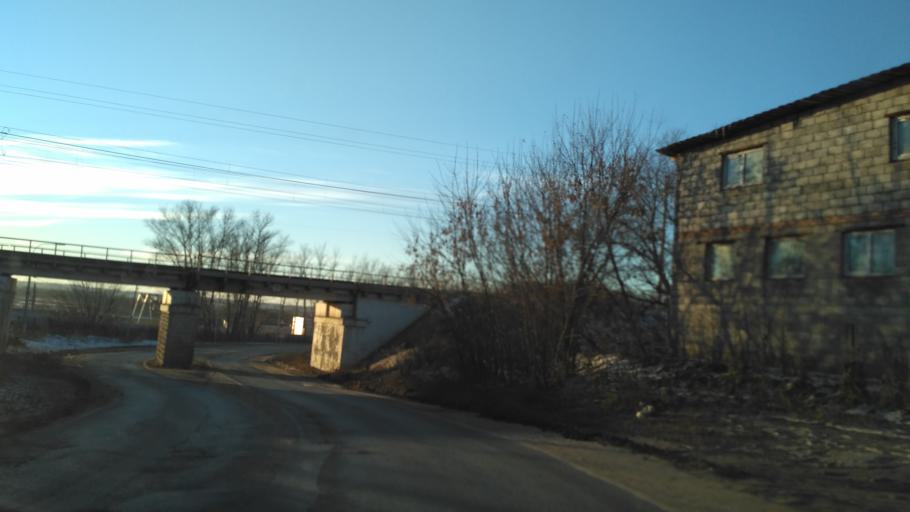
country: RU
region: Tula
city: Gorelki
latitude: 54.2229
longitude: 37.5884
